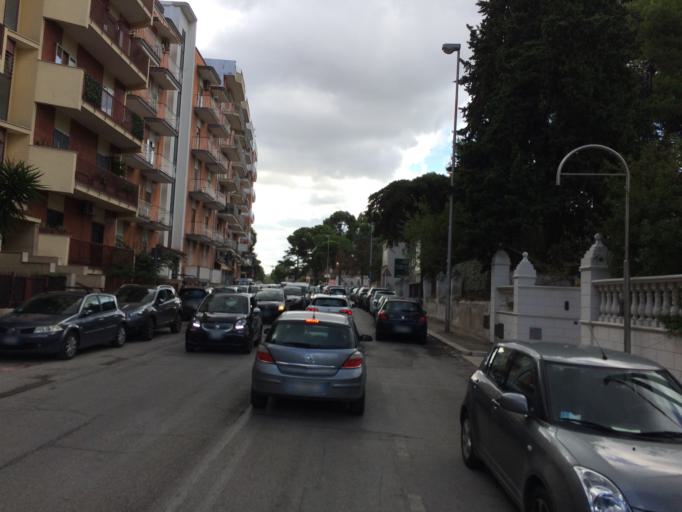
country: IT
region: Apulia
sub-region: Provincia di Bari
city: Bari
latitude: 41.1005
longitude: 16.8799
